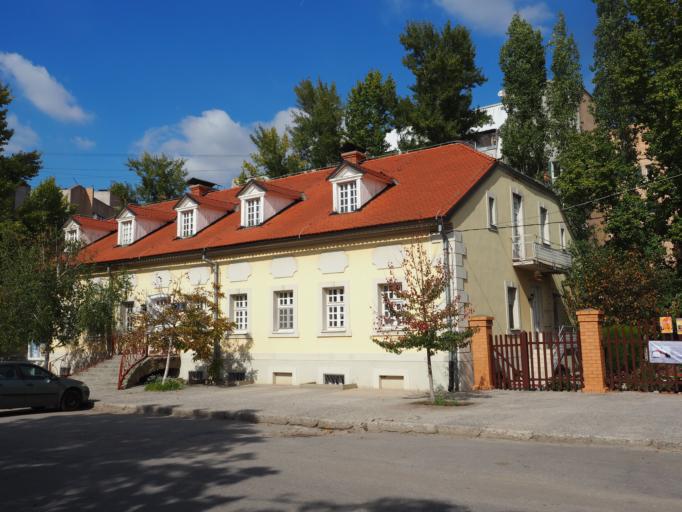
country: RU
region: Volgograd
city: Krasnoslobodsk
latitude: 48.5123
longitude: 44.5497
